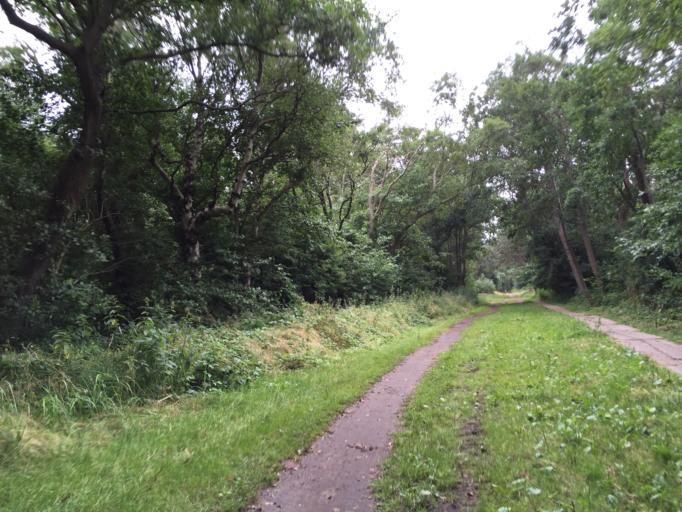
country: DE
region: Mecklenburg-Vorpommern
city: Hiddensee
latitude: 54.5191
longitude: 13.0818
